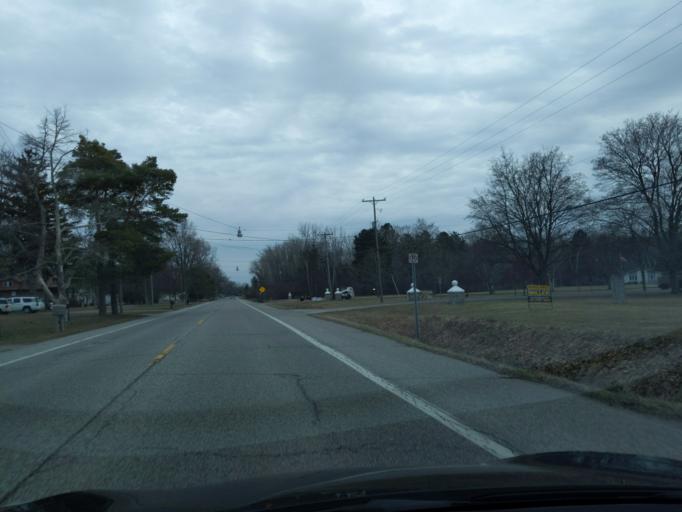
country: US
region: Michigan
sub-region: Bay County
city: Bay City
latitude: 43.6579
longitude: -83.9125
